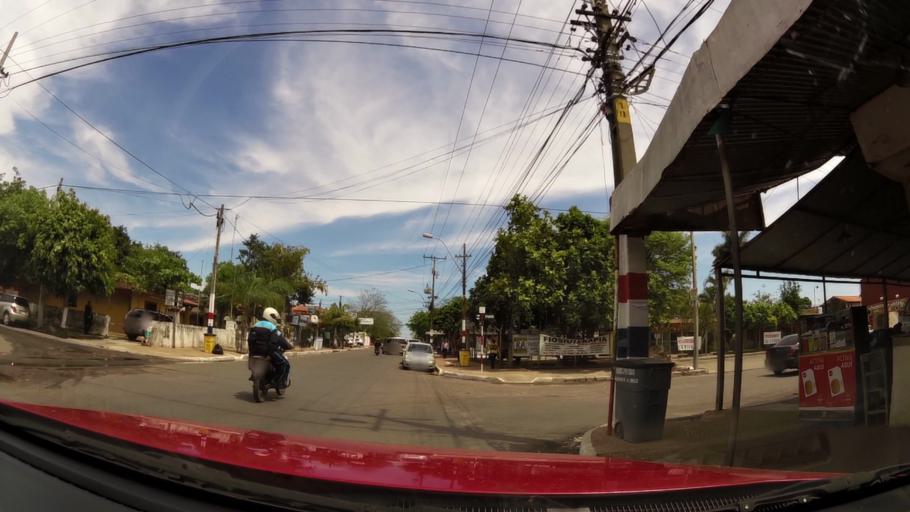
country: PY
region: Central
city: Colonia Mariano Roque Alonso
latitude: -25.2127
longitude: -57.5317
